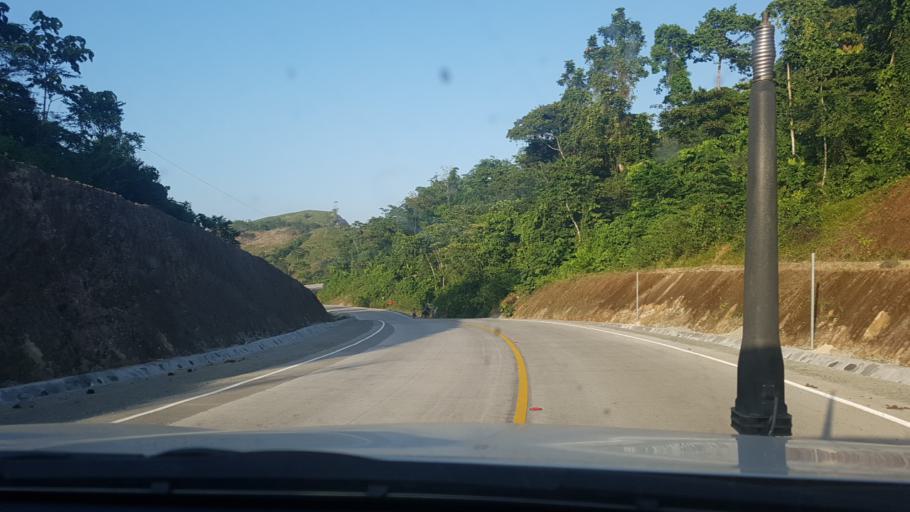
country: NI
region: Atlantico Sur
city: Rama
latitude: 11.8244
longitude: -84.0857
